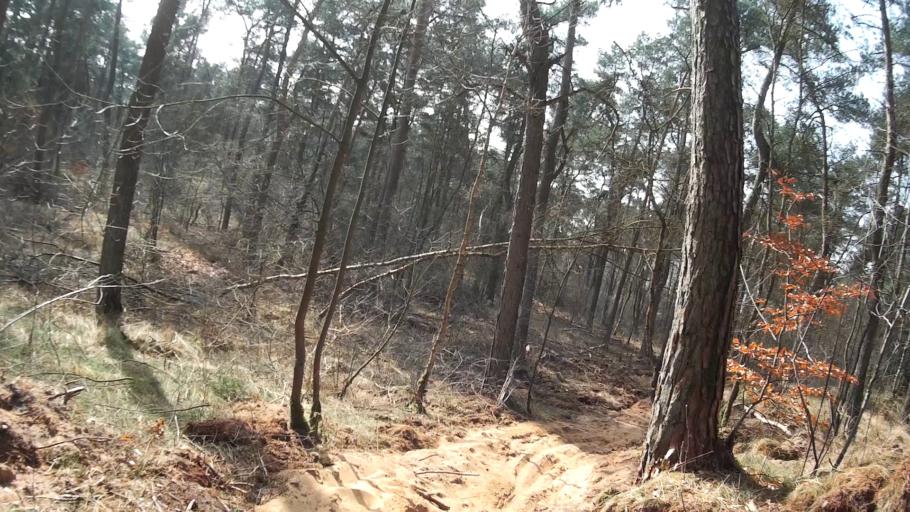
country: NL
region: Utrecht
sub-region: Gemeente Utrechtse Heuvelrug
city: Driebergen-Rijsenburg
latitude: 52.0705
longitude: 5.3127
